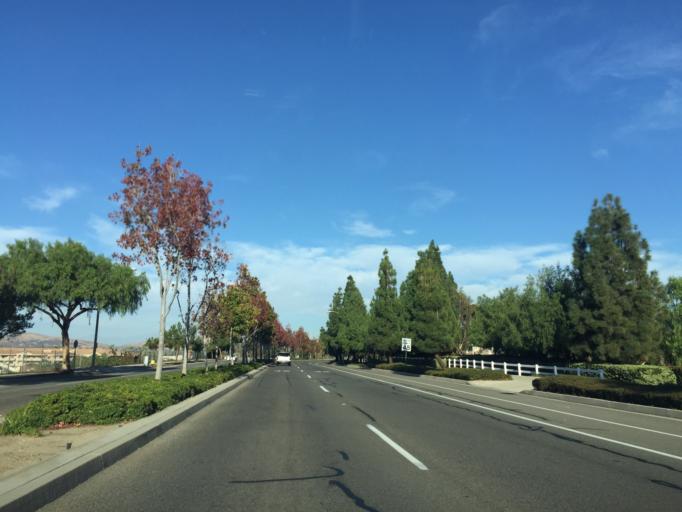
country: US
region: California
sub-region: Orange County
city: Fullerton
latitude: 33.8940
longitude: -117.9153
